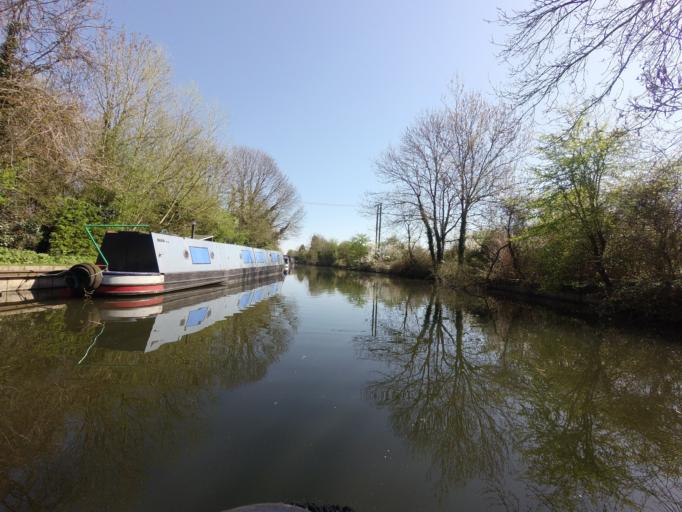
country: GB
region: England
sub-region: Hertfordshire
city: Rickmansworth
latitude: 51.6316
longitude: -0.4767
